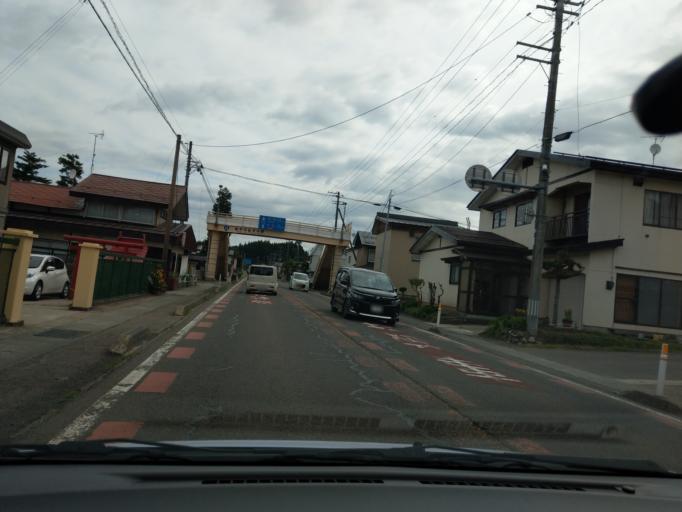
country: JP
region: Akita
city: Yokotemachi
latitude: 39.3688
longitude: 140.5679
